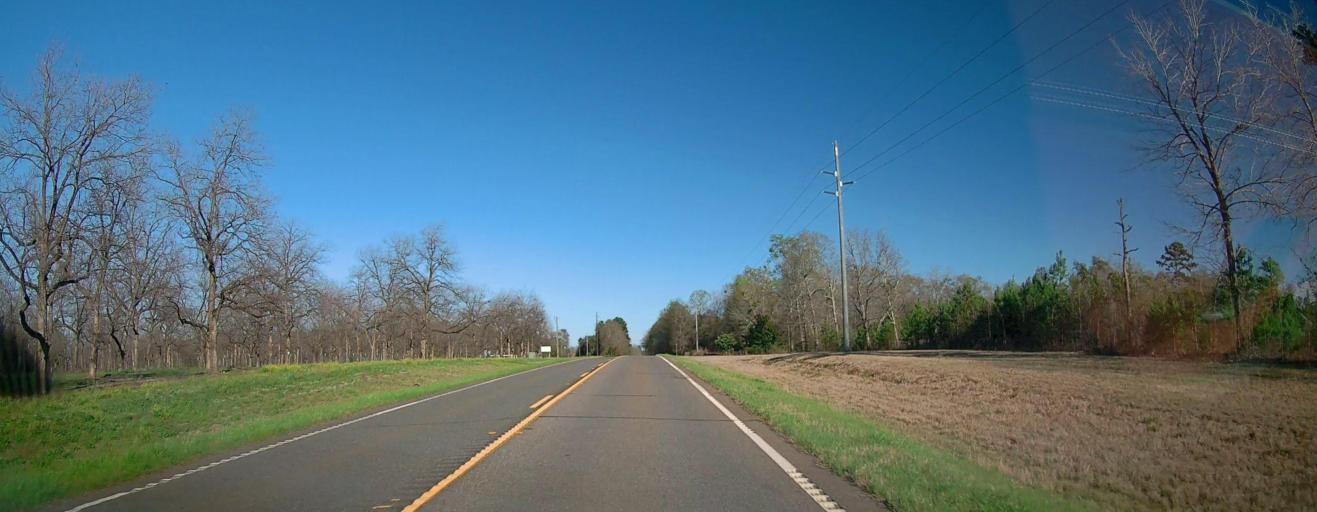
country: US
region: Georgia
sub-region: Macon County
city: Marshallville
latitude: 32.4394
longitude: -83.8573
